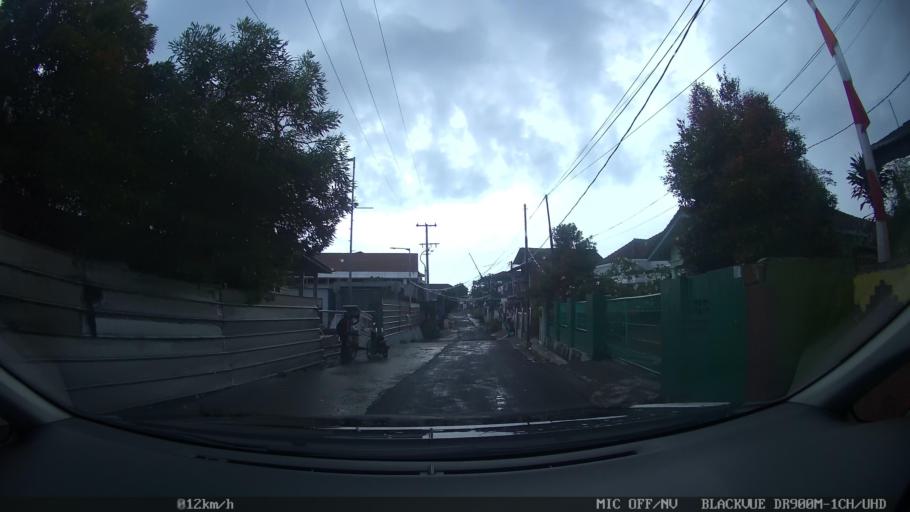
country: ID
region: Lampung
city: Kedaton
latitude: -5.3998
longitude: 105.2860
